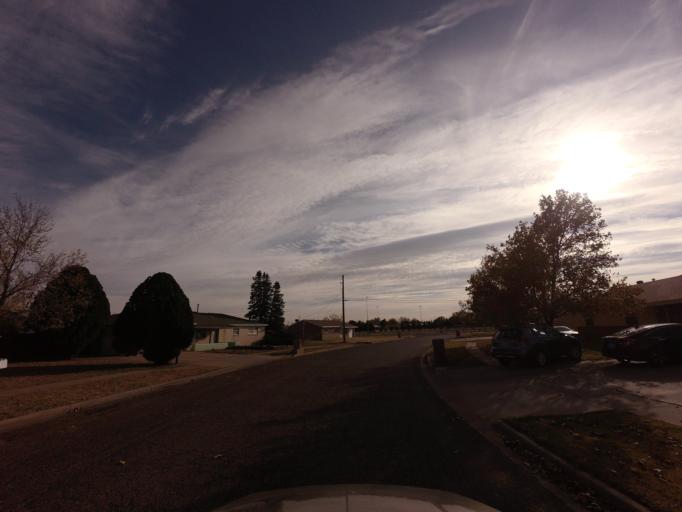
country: US
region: New Mexico
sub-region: Curry County
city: Clovis
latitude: 34.4262
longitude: -103.2264
